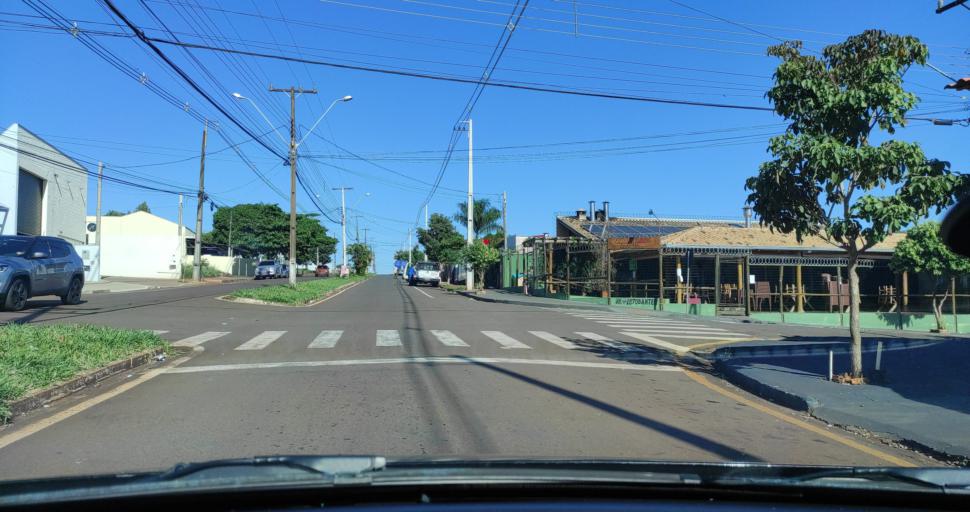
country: BR
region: Parana
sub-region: Ibipora
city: Ibipora
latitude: -23.2748
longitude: -51.0677
